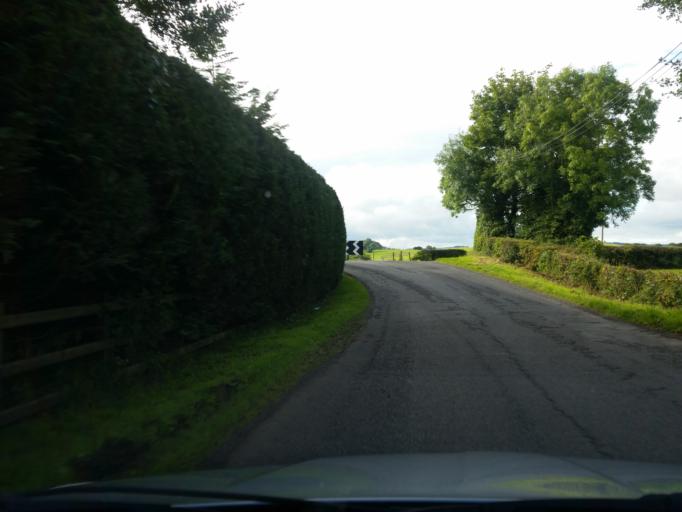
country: IE
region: Ulster
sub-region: County Monaghan
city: Clones
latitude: 54.1951
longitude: -7.2518
